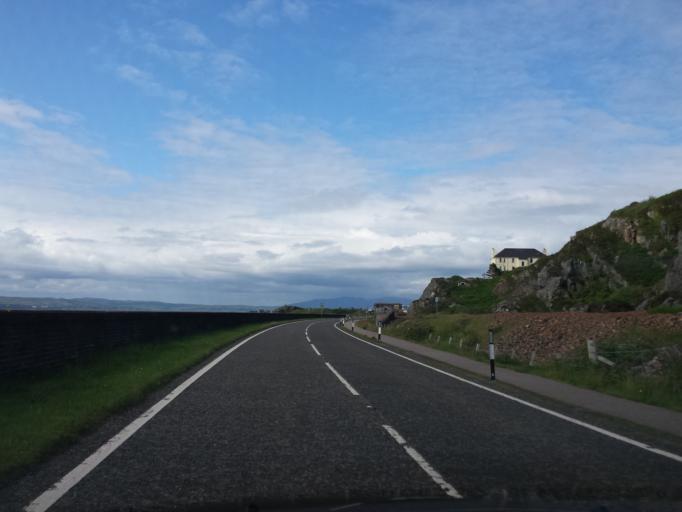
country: GB
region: Scotland
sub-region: Highland
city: Portree
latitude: 57.0005
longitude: -5.8337
